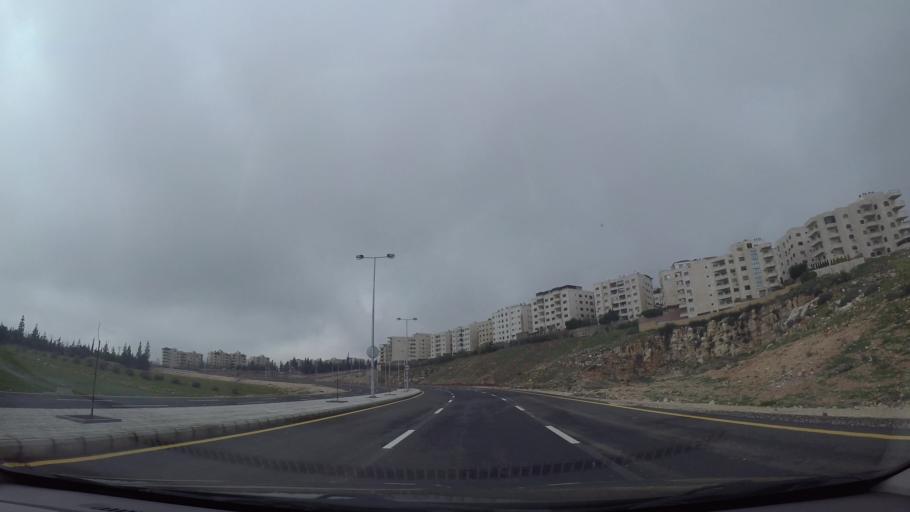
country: JO
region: Amman
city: Wadi as Sir
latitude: 31.9351
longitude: 35.8579
